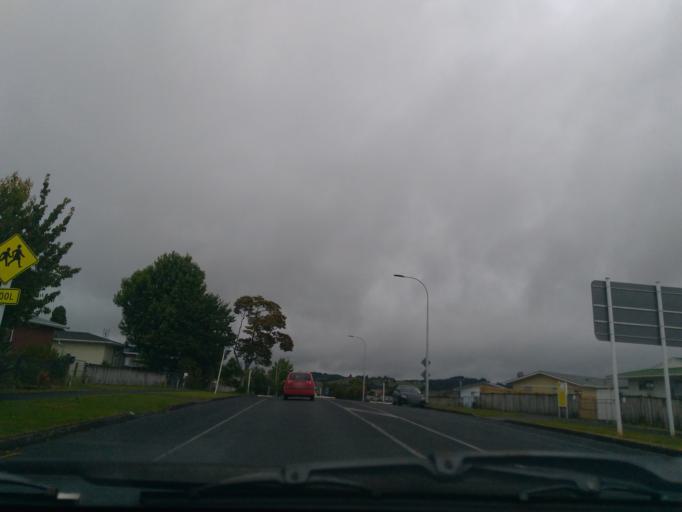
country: NZ
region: Northland
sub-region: Whangarei
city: Whangarei
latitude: -35.6859
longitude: 174.3264
